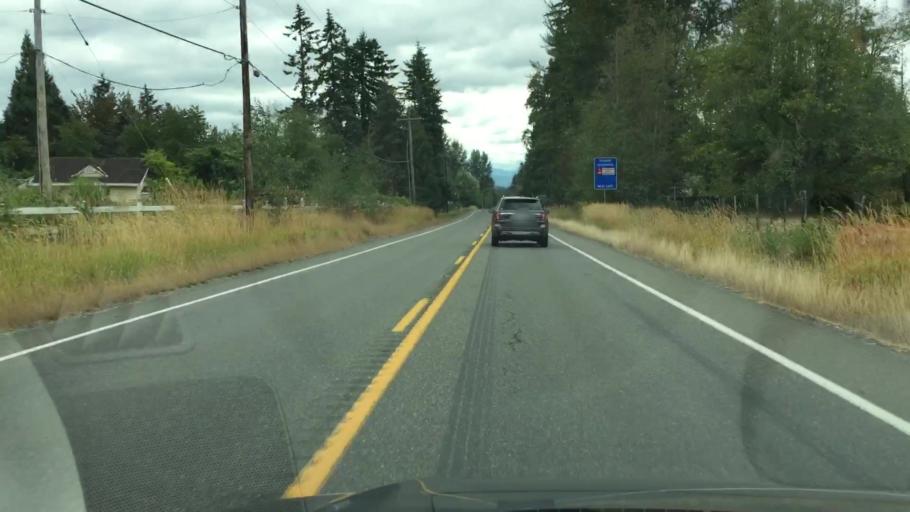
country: US
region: Washington
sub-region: Pierce County
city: Graham
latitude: 47.0202
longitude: -122.2963
